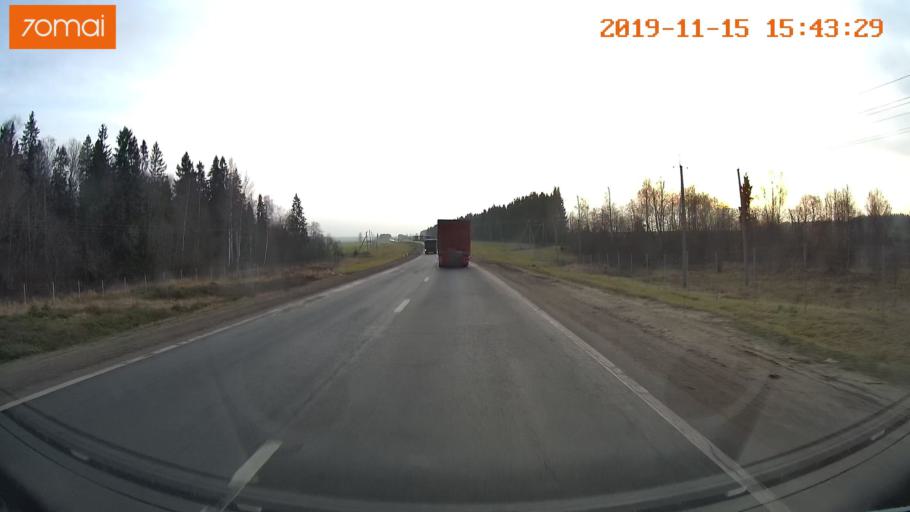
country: RU
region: Jaroslavl
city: Danilov
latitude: 57.9818
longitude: 40.0275
